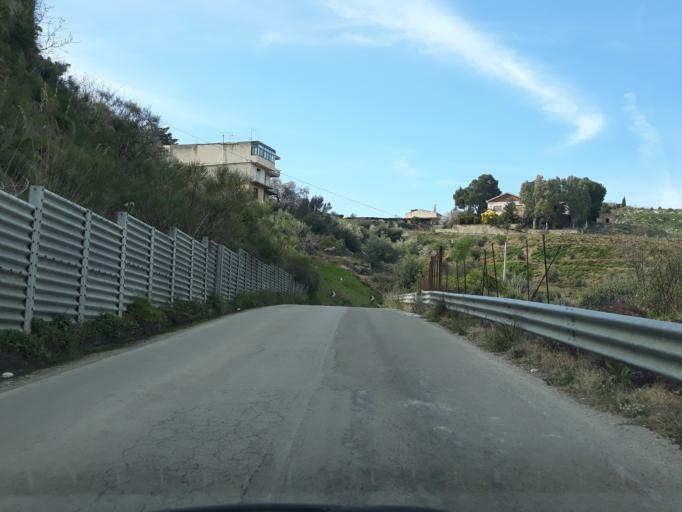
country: IT
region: Sicily
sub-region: Palermo
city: Altofonte
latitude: 38.0409
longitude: 13.3099
